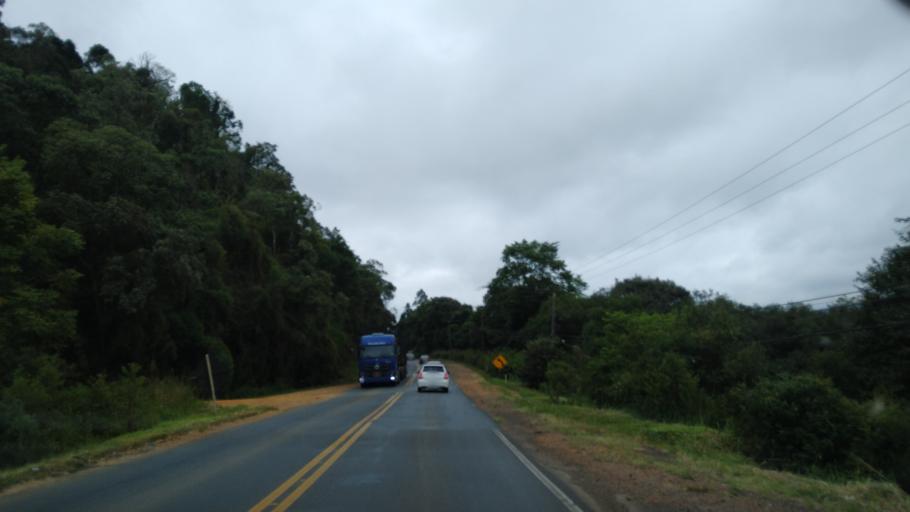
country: BR
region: Parana
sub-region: Uniao Da Vitoria
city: Uniao da Vitoria
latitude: -26.2294
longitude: -51.1274
